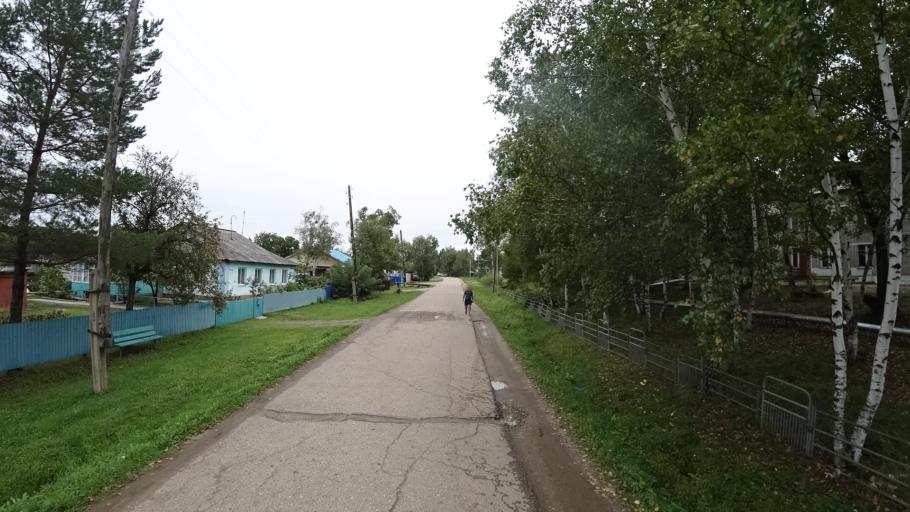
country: RU
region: Primorskiy
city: Monastyrishche
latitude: 44.0829
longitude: 132.5814
